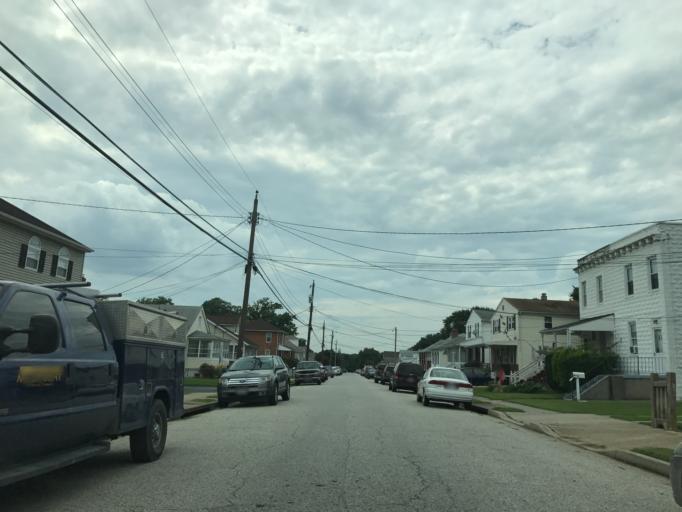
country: US
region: Maryland
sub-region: Baltimore County
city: Essex
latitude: 39.3129
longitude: -76.4793
